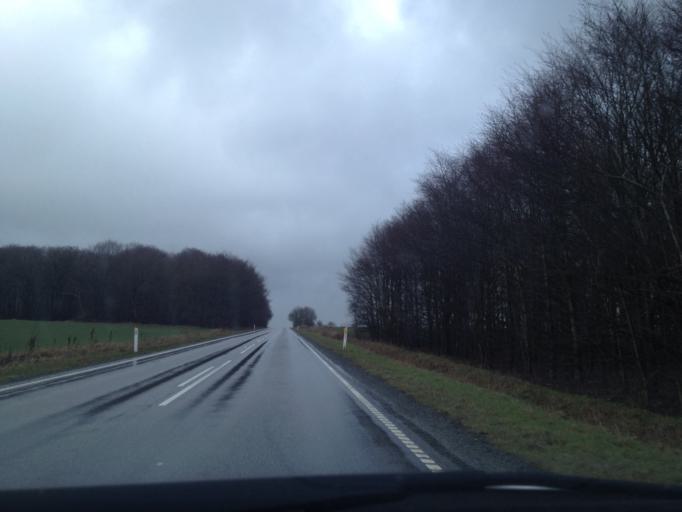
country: DK
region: South Denmark
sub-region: Vejen Kommune
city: Rodding
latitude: 55.3587
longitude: 9.1437
